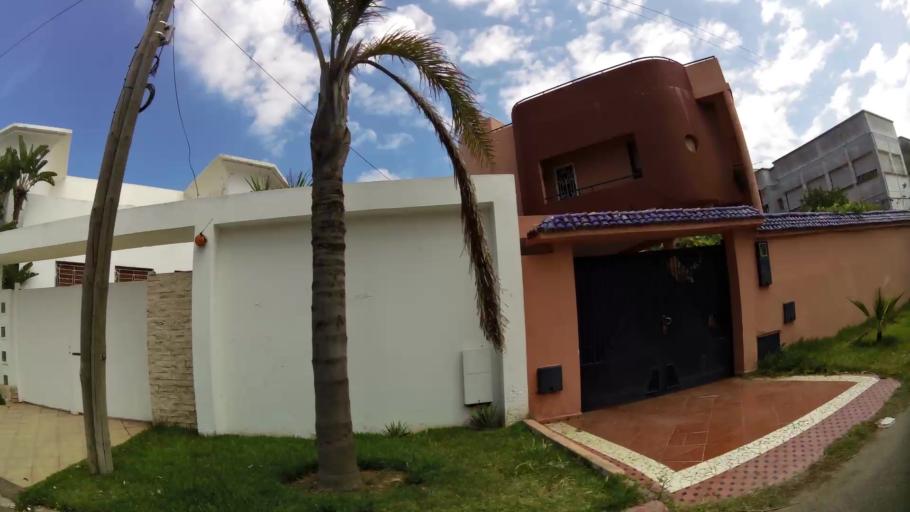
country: MA
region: Gharb-Chrarda-Beni Hssen
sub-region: Kenitra Province
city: Kenitra
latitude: 34.2648
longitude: -6.5975
